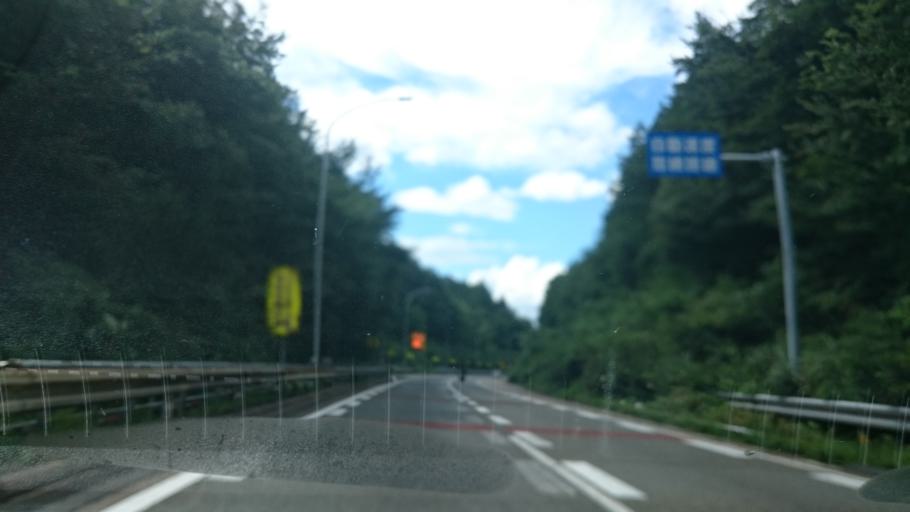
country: JP
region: Gifu
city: Nakatsugawa
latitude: 35.5054
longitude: 137.5918
